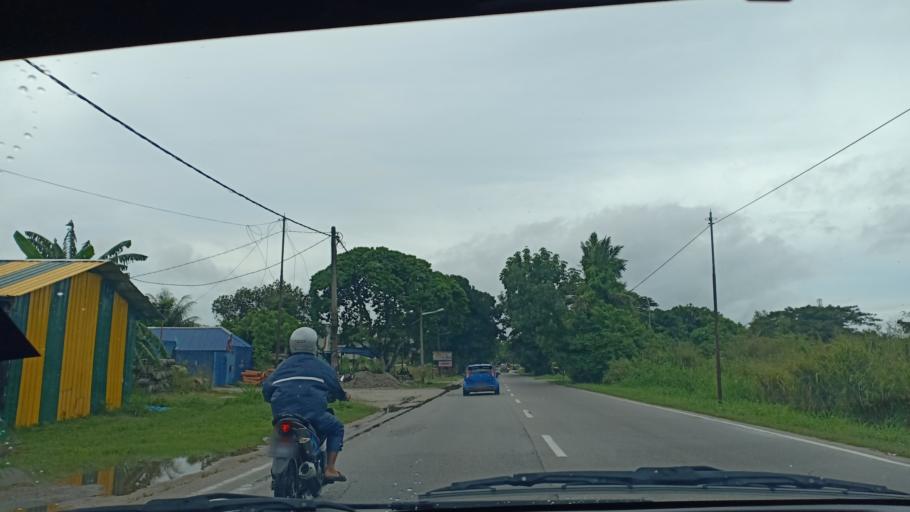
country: MY
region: Penang
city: Kepala Batas
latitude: 5.4931
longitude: 100.4539
